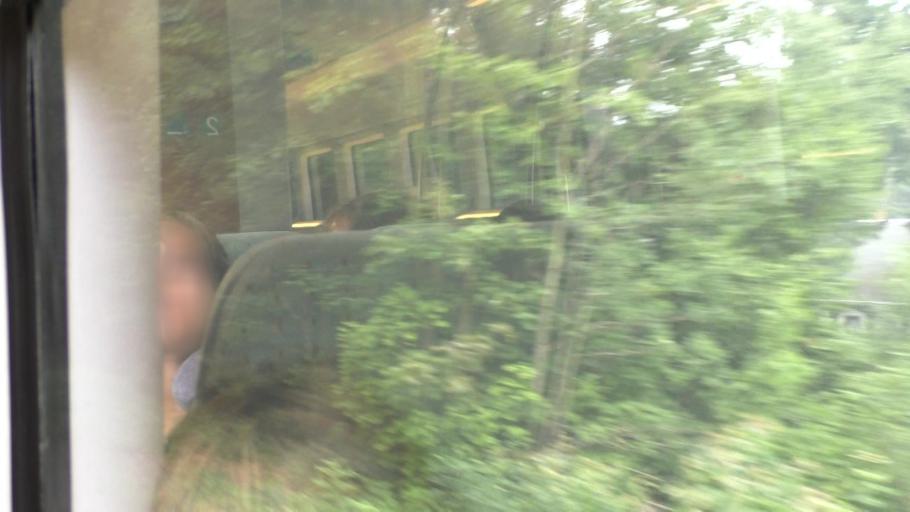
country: DE
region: Saxony
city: Neugersdorf
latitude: 50.9871
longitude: 14.6015
